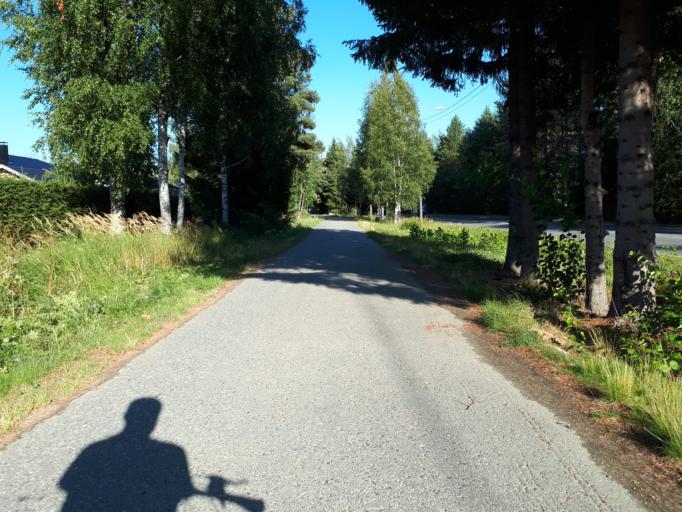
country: FI
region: Northern Ostrobothnia
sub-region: Oulunkaari
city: Ii
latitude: 65.3162
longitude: 25.3922
